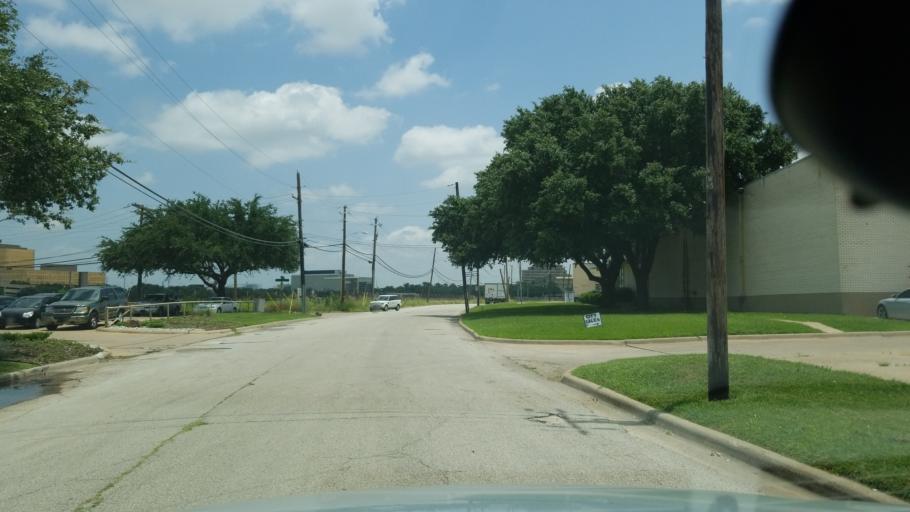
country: US
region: Texas
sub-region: Dallas County
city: Irving
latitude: 32.8296
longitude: -96.8787
